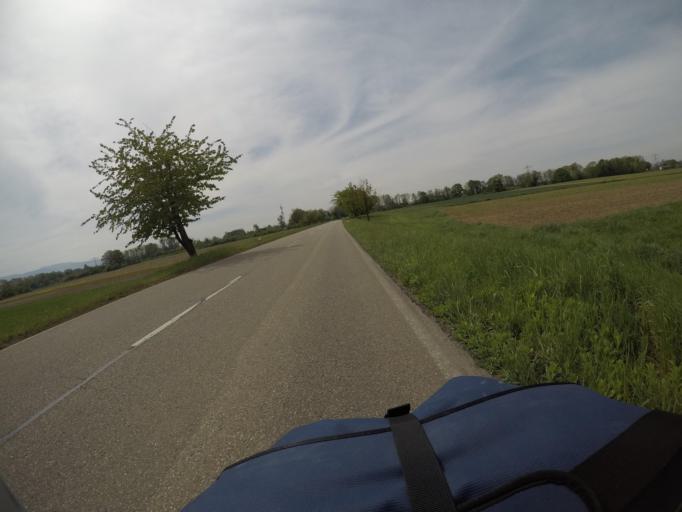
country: DE
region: Baden-Wuerttemberg
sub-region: Karlsruhe Region
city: Schwarzach
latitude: 48.7555
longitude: 8.0391
